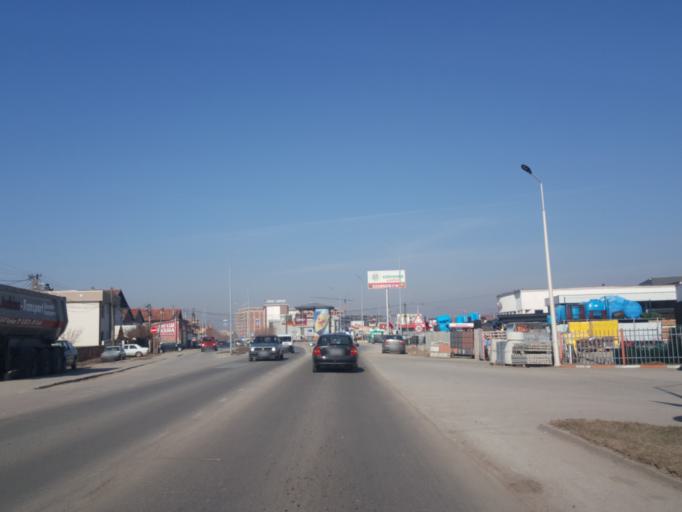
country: XK
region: Mitrovica
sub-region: Vushtrri
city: Vushtrri
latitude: 42.8138
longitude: 20.9841
